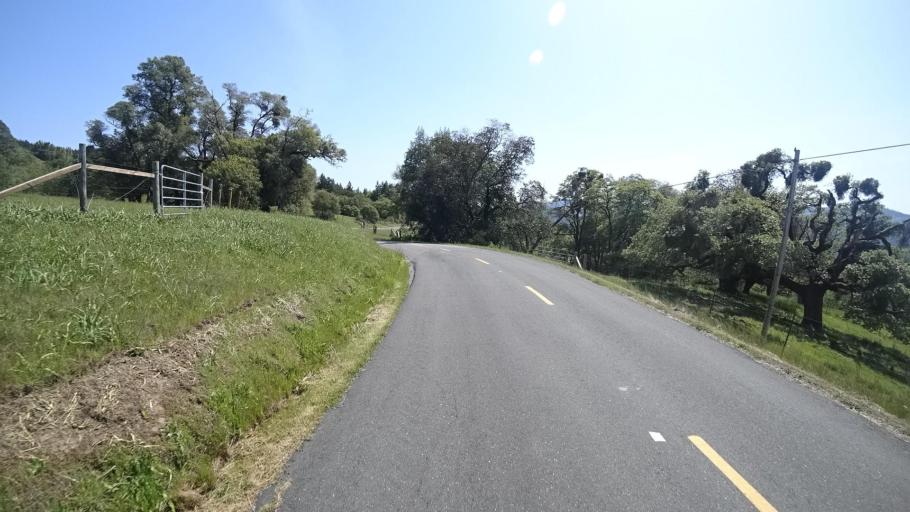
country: US
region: California
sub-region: Humboldt County
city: Redway
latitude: 40.2544
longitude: -123.6246
